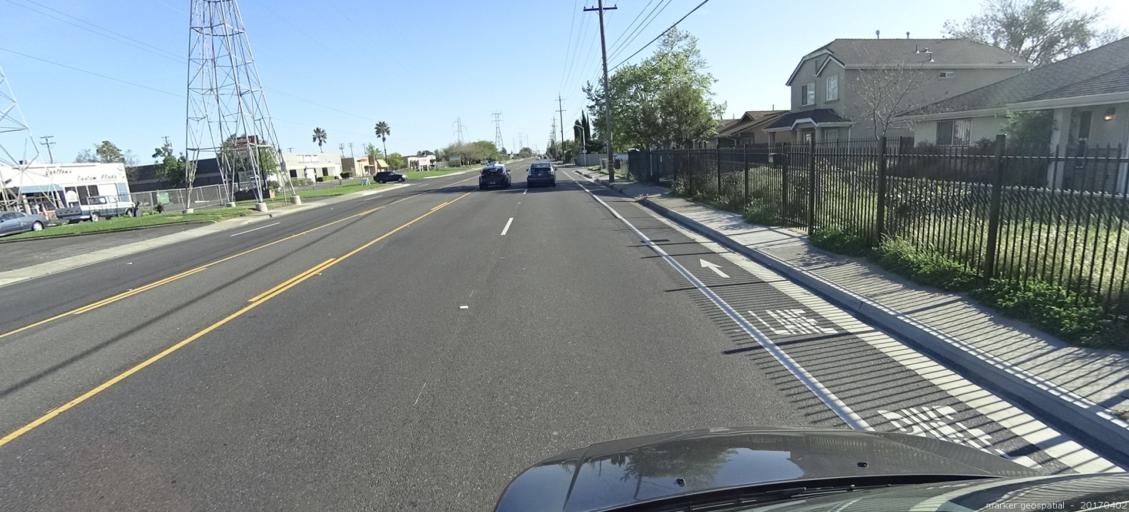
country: US
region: California
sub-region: Sacramento County
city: Florin
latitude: 38.5213
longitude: -121.4092
